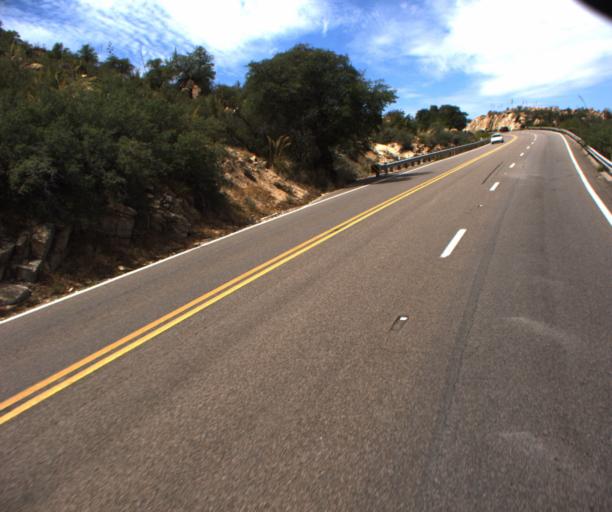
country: US
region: Arizona
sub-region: Gila County
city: Miami
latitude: 33.3660
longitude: -110.9690
